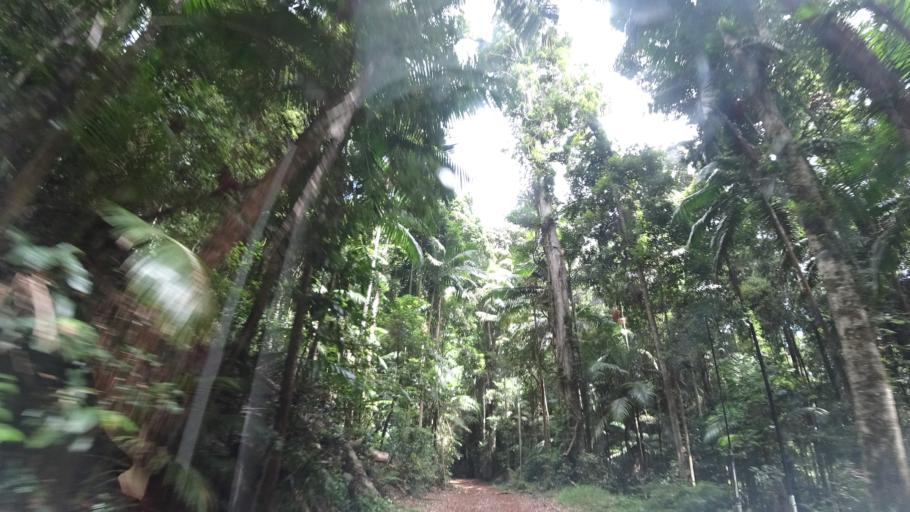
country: AU
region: Queensland
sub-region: Moreton Bay
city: Highvale
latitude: -27.3319
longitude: 152.7623
